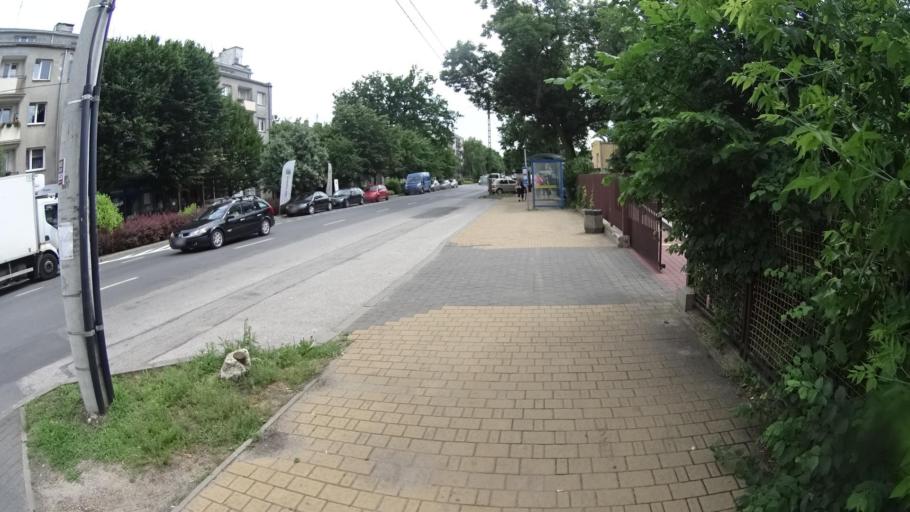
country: PL
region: Masovian Voivodeship
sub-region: Powiat grojecki
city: Grojec
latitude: 51.8643
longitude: 20.8669
